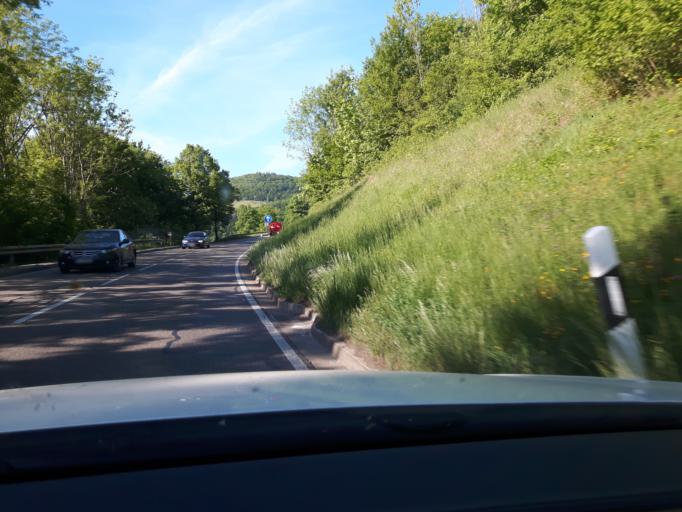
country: DE
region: Baden-Wuerttemberg
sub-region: Tuebingen Region
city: Pfullingen
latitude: 48.4365
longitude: 9.2609
